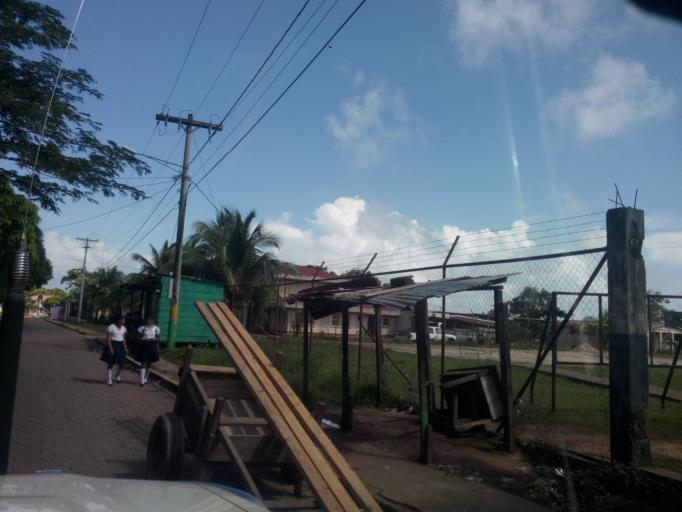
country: NI
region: Atlantico Norte (RAAN)
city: Puerto Cabezas
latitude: 14.0354
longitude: -83.3752
